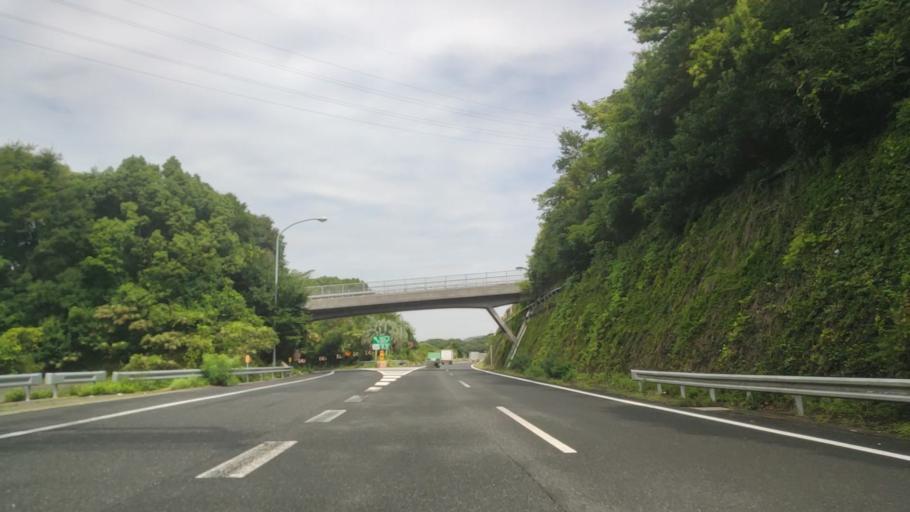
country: JP
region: Wakayama
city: Kainan
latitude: 34.1425
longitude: 135.2106
